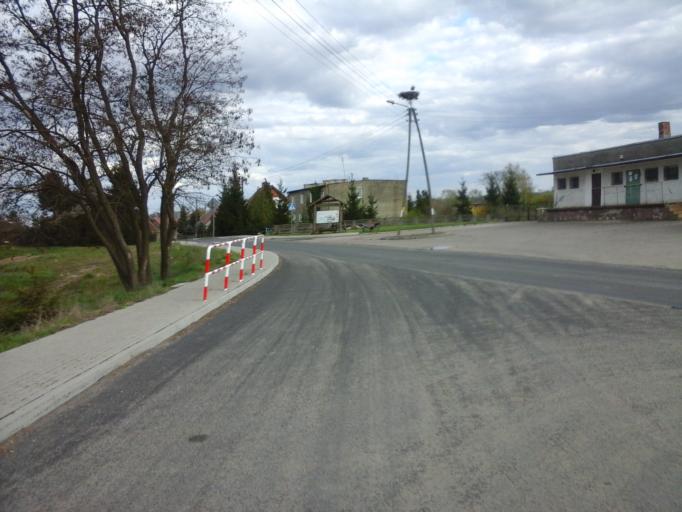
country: PL
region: West Pomeranian Voivodeship
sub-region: Powiat choszczenski
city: Krzecin
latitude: 53.0852
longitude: 15.5475
